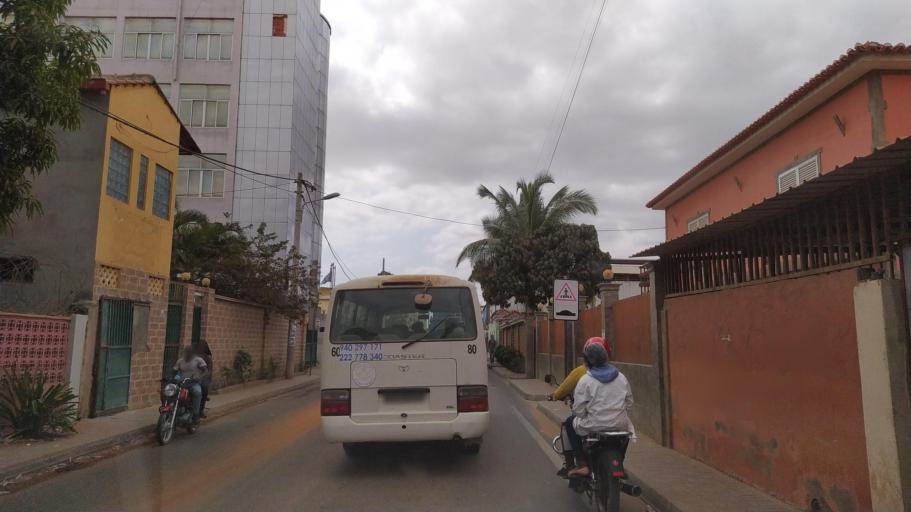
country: AO
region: Luanda
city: Luanda
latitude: -8.9650
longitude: 13.1534
